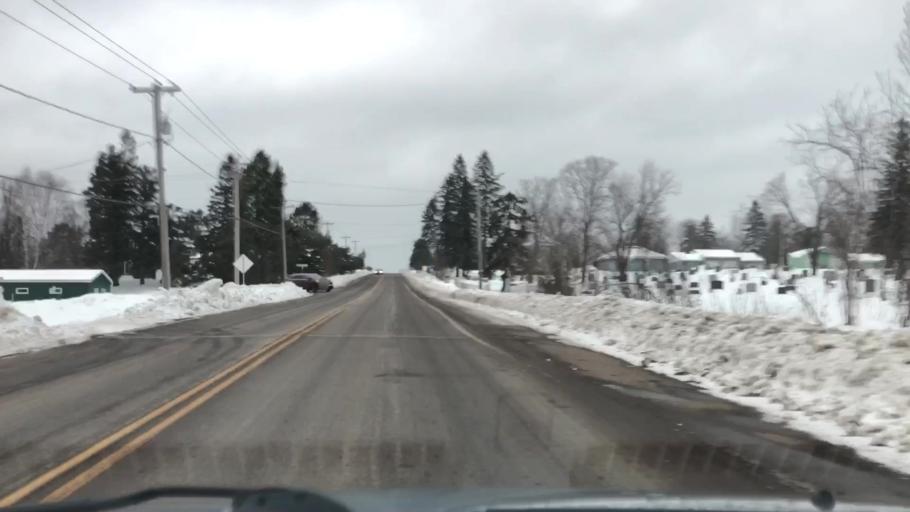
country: US
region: Minnesota
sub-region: Saint Louis County
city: Arnold
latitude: 46.8588
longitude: -92.1111
